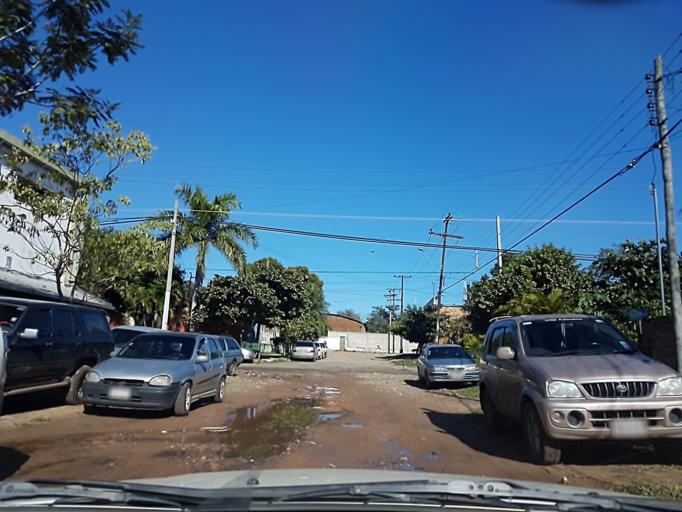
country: PY
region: Asuncion
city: Asuncion
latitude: -25.2536
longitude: -57.5822
